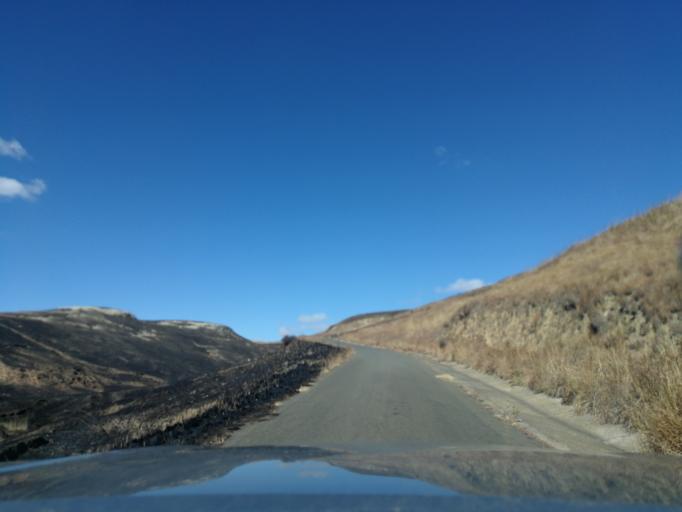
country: ZA
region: Orange Free State
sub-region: Thabo Mofutsanyana District Municipality
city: Phuthaditjhaba
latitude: -28.5120
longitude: 28.6260
